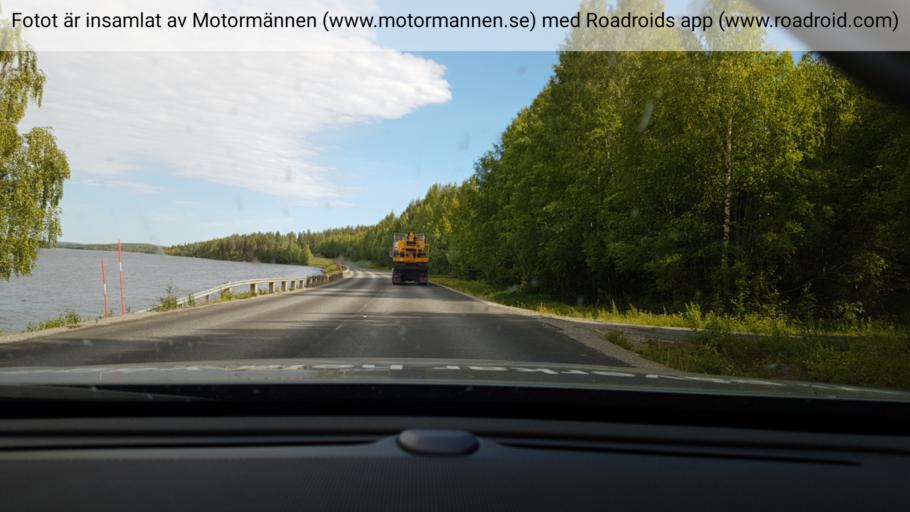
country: SE
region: Vaesterbotten
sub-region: Lycksele Kommun
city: Soderfors
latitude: 64.8448
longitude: 17.9691
